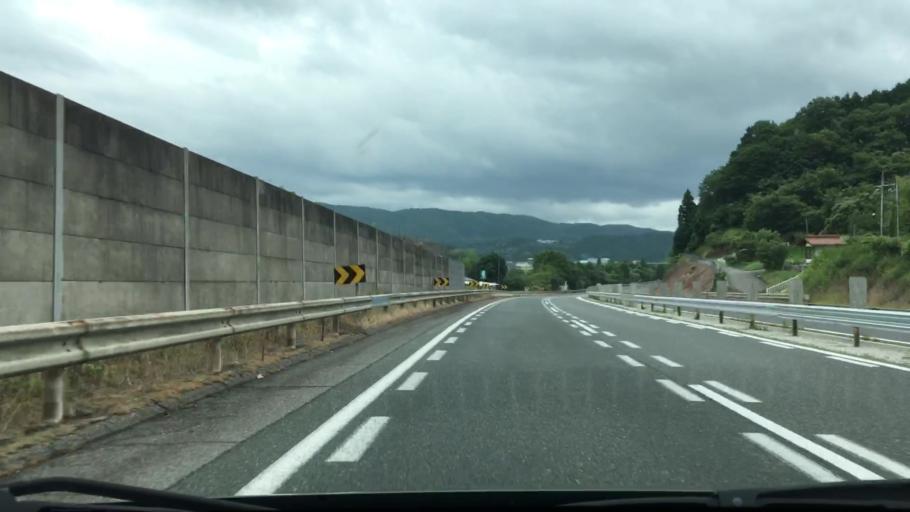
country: JP
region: Okayama
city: Niimi
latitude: 34.9497
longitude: 133.3297
